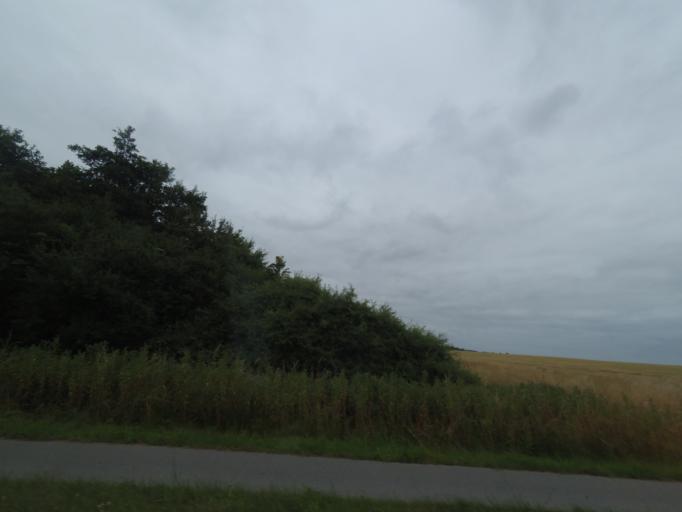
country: DK
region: South Denmark
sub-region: Nordfyns Kommune
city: Otterup
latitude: 55.5220
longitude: 10.4141
